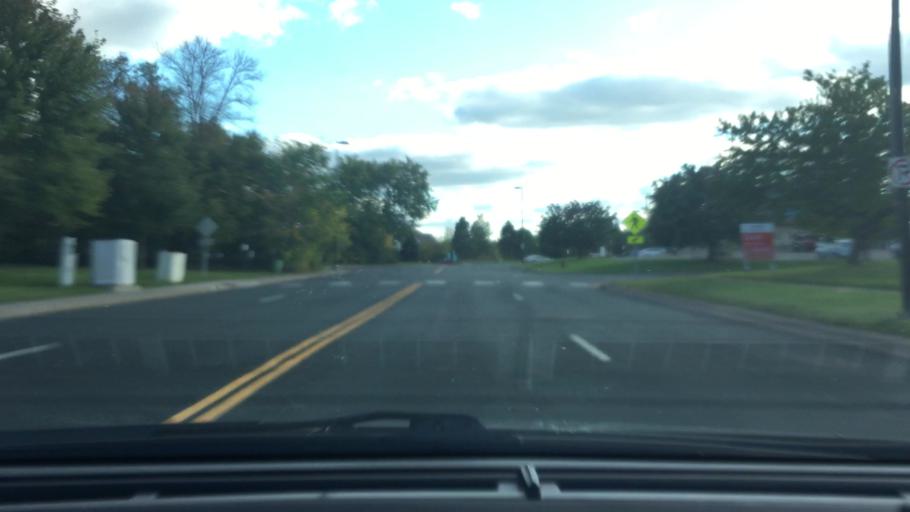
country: US
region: Minnesota
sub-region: Hennepin County
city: Maple Grove
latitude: 45.0662
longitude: -93.4397
